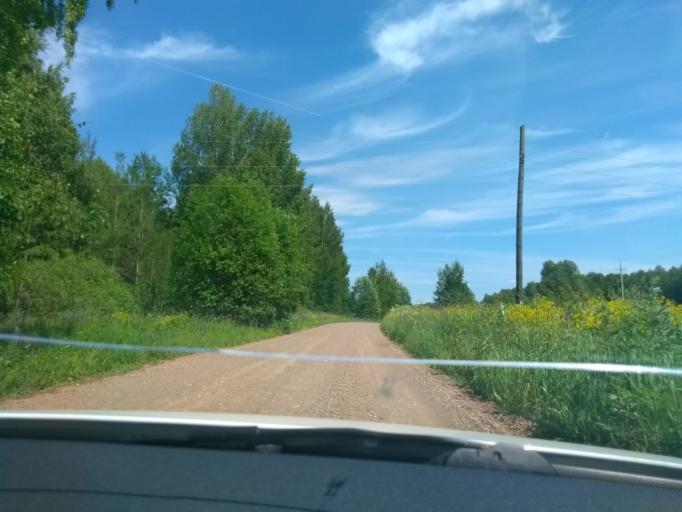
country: RU
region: Perm
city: Sylva
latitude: 57.8170
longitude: 56.7301
